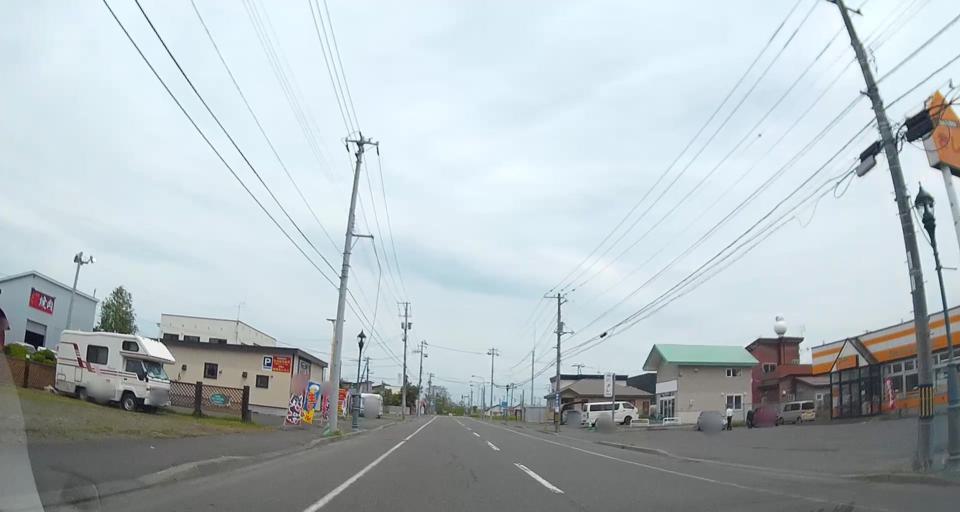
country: JP
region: Hokkaido
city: Chitose
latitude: 42.7670
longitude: 141.8194
